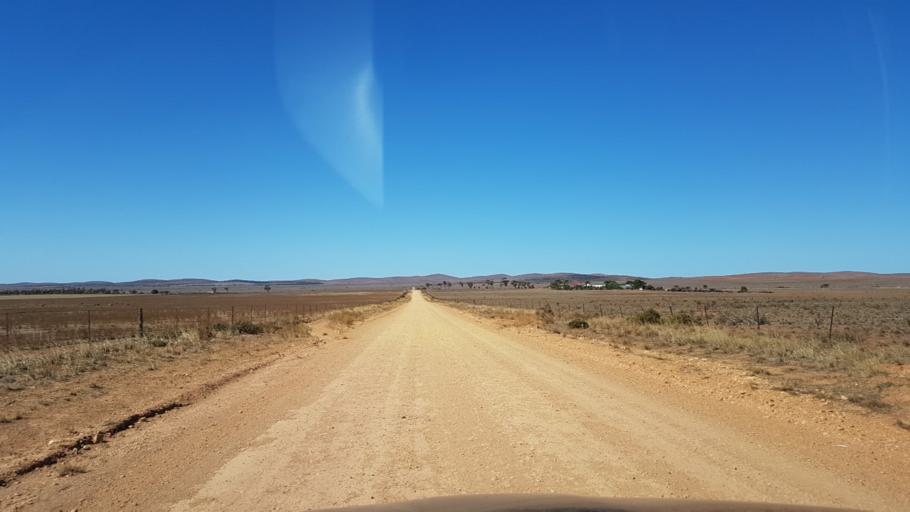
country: AU
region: South Australia
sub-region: Peterborough
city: Peterborough
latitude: -32.9917
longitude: 138.8363
